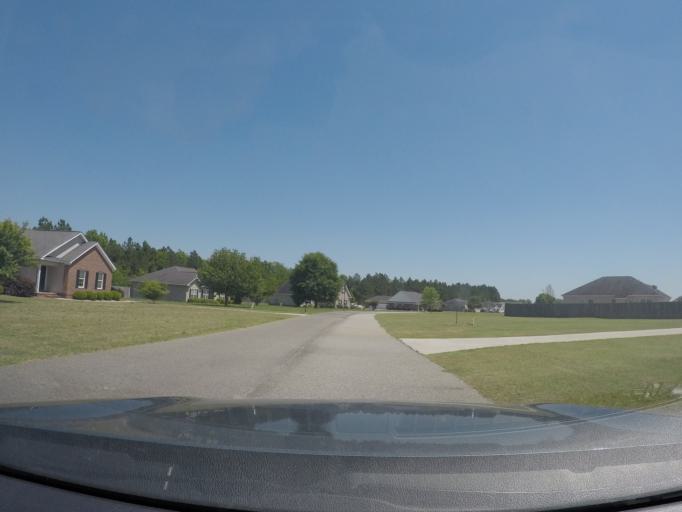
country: US
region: Georgia
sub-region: Bulloch County
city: Brooklet
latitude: 32.3598
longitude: -81.7541
